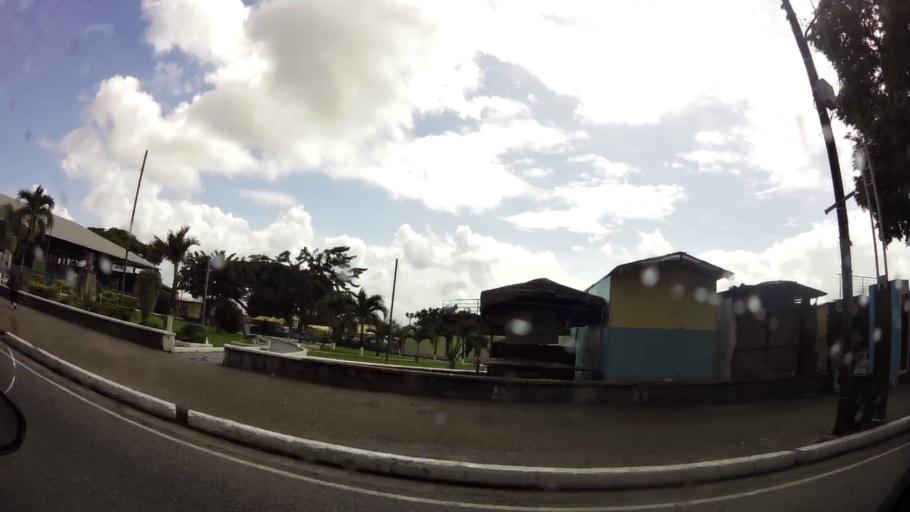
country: TT
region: Borough of Arima
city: Arima
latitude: 10.6390
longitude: -61.2819
